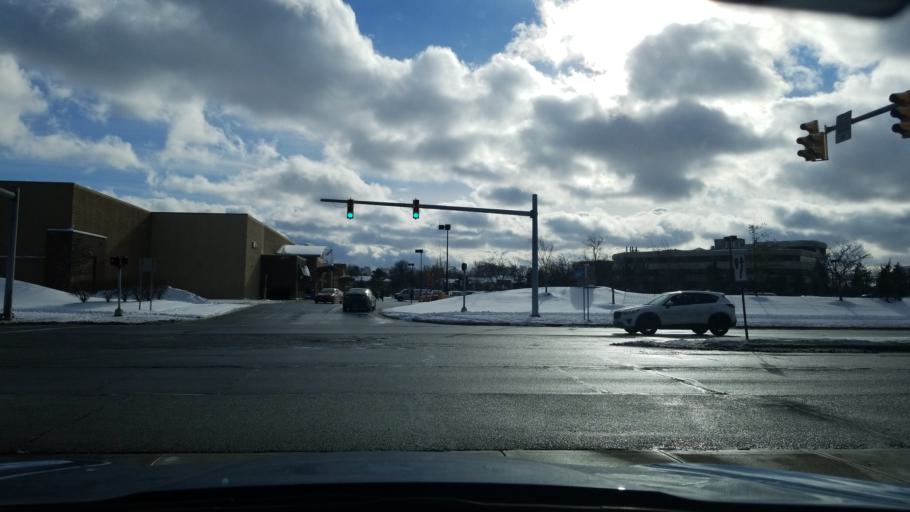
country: US
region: Ohio
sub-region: Cuyahoga County
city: North Olmsted
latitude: 41.4190
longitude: -81.8977
